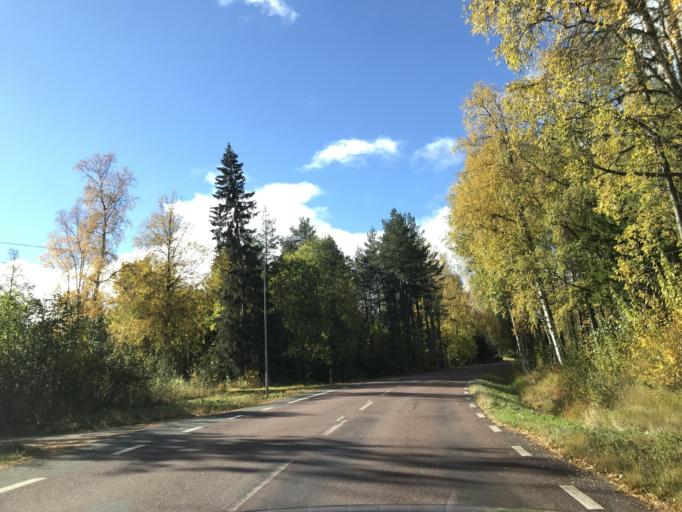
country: NO
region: Hedmark
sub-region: Trysil
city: Innbygda
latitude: 61.6885
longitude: 13.1366
